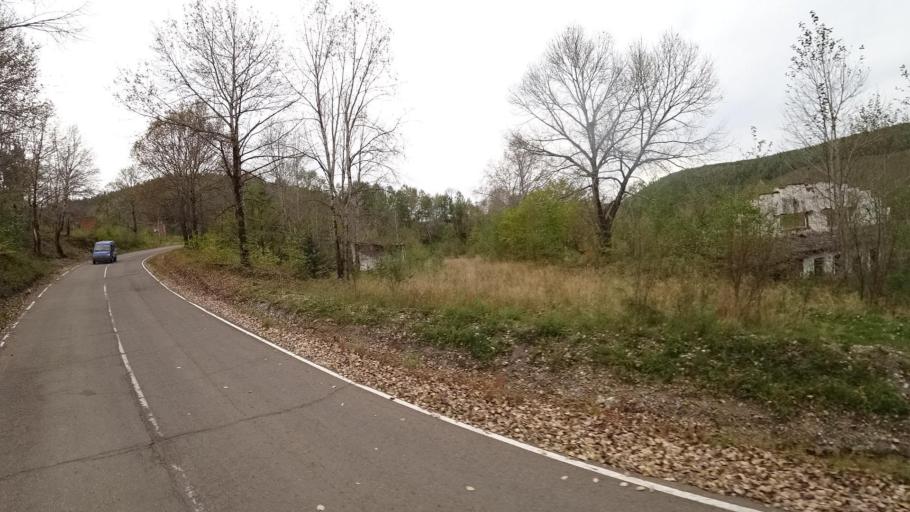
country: RU
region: Jewish Autonomous Oblast
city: Khingansk
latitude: 49.1239
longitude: 131.1892
